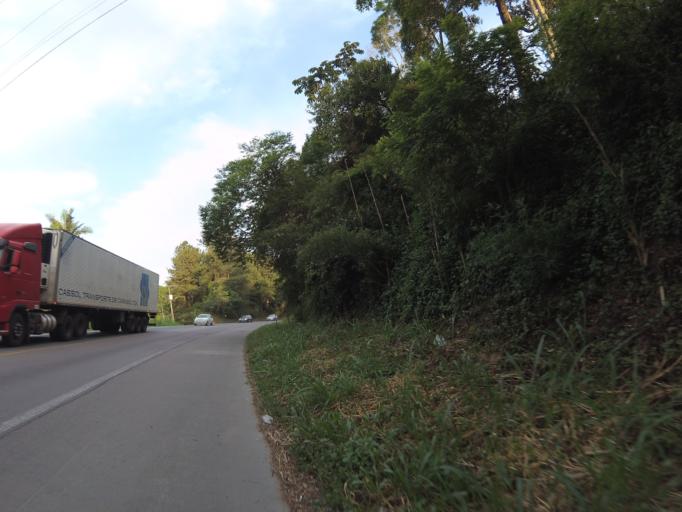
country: BR
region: Santa Catarina
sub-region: Indaial
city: Indaial
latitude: -26.8828
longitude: -49.1544
